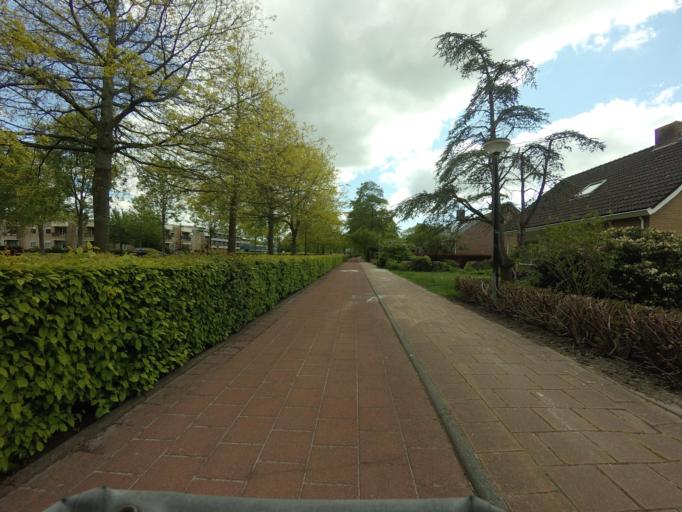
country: NL
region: Friesland
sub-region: Sudwest Fryslan
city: Bolsward
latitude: 53.0678
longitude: 5.5301
